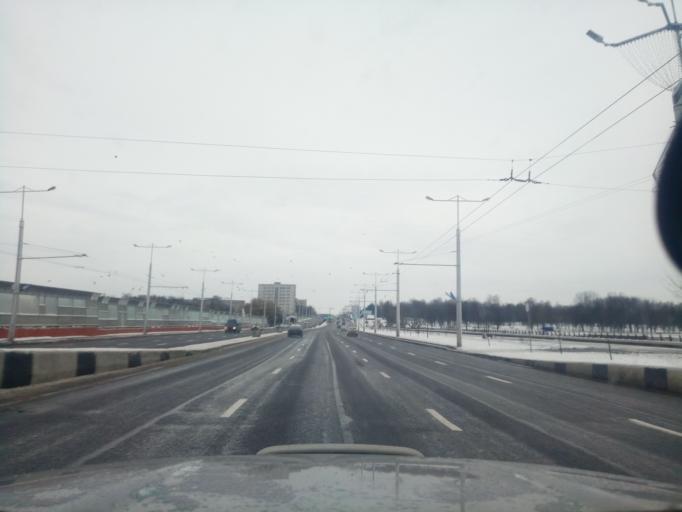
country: BY
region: Minsk
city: Hatava
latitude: 53.8529
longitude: 27.6339
